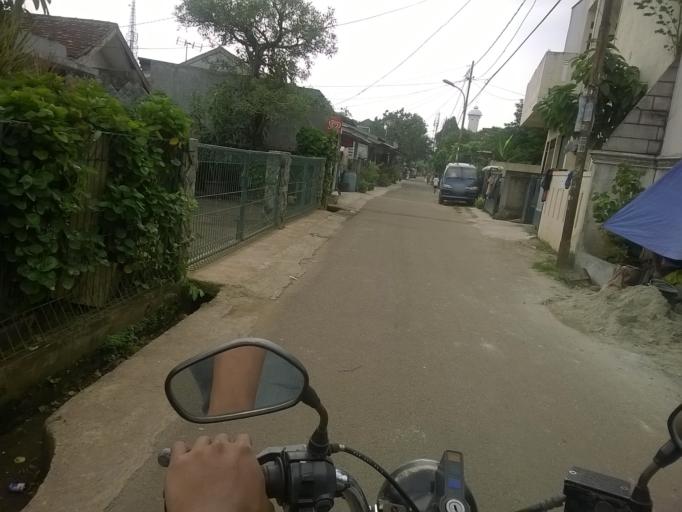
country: ID
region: West Java
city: Pamulang
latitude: -6.3130
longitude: 106.7795
